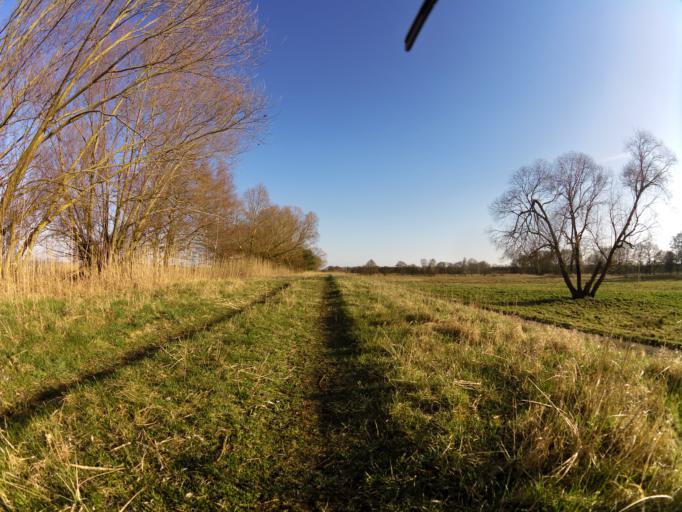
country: PL
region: West Pomeranian Voivodeship
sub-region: Powiat policki
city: Nowe Warpno
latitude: 53.7173
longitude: 14.3417
